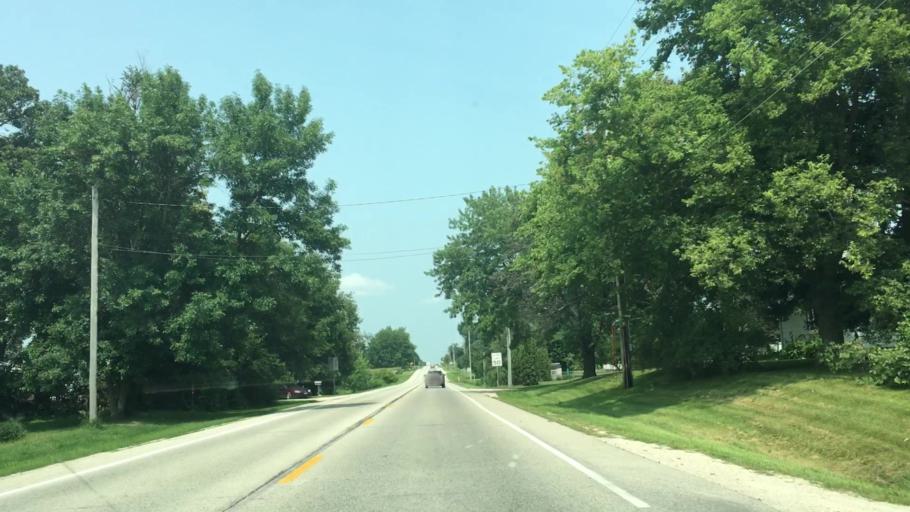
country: US
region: Iowa
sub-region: Buchanan County
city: Independence
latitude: 42.4835
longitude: -91.8894
